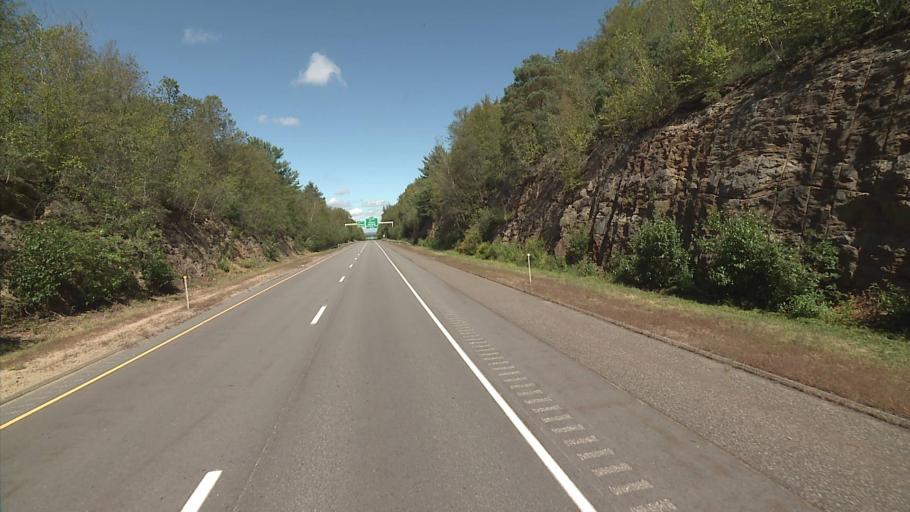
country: US
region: Connecticut
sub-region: New London County
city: Colchester
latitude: 41.5467
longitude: -72.3159
